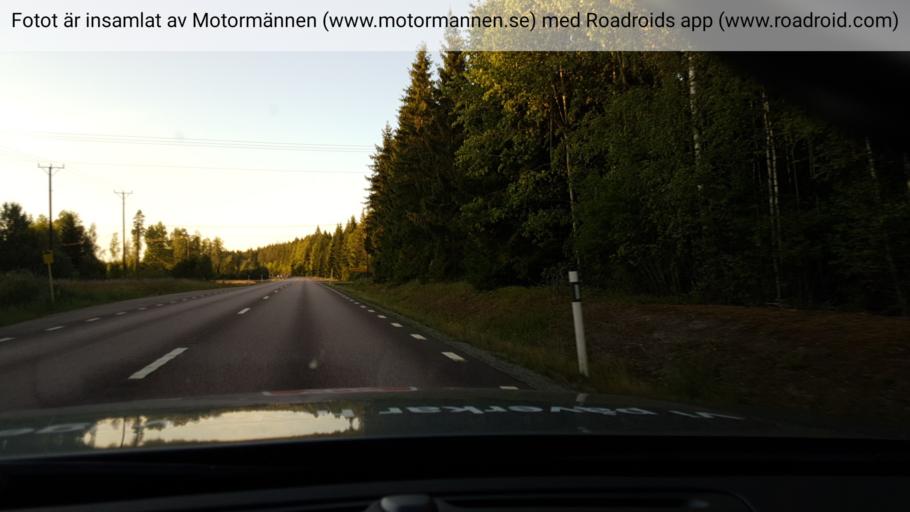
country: SE
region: OErebro
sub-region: Karlskoga Kommun
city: Karlskoga
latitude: 59.4198
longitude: 14.4275
